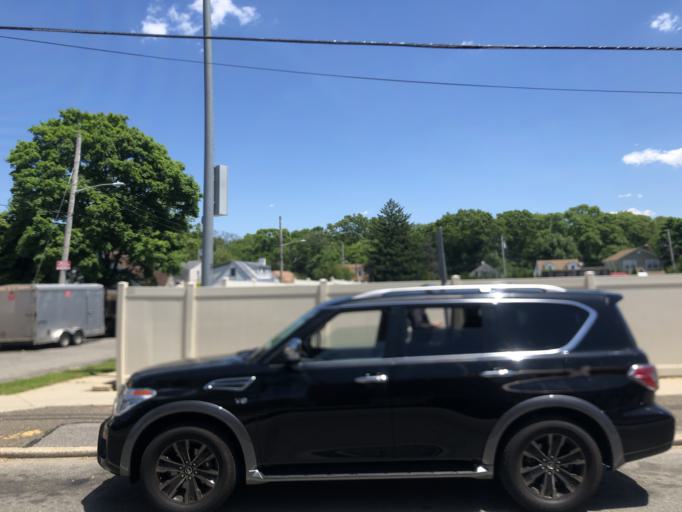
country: US
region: New York
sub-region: Nassau County
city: Freeport
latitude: 40.6669
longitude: -73.5737
